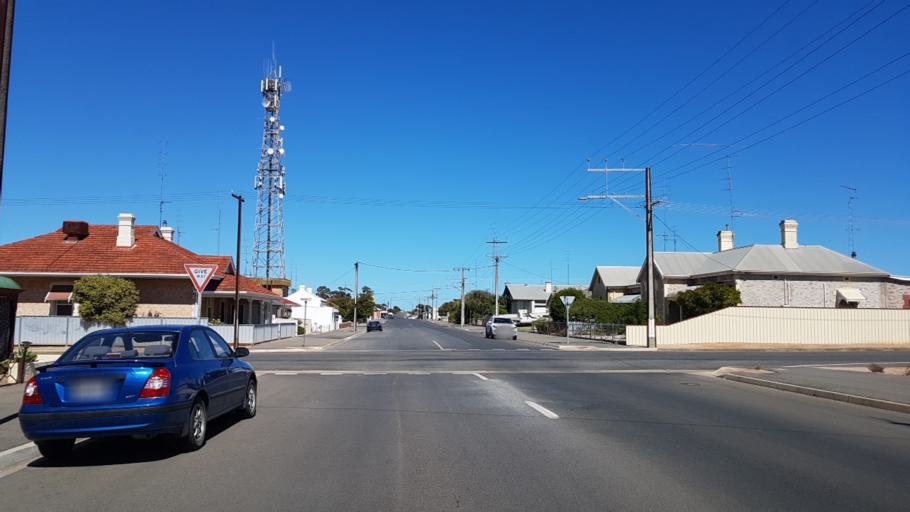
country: AU
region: South Australia
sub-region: Copper Coast
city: Kadina
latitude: -33.9635
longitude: 137.7190
